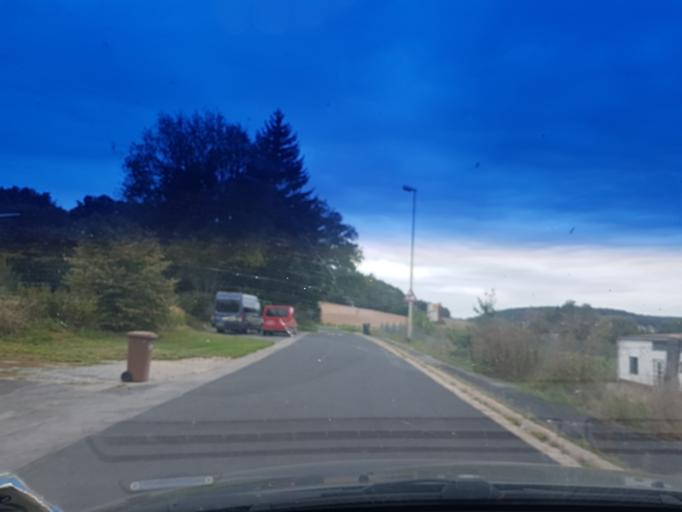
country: DE
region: Bavaria
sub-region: Regierungsbezirk Unterfranken
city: Geiselwind
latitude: 49.8406
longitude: 10.5147
